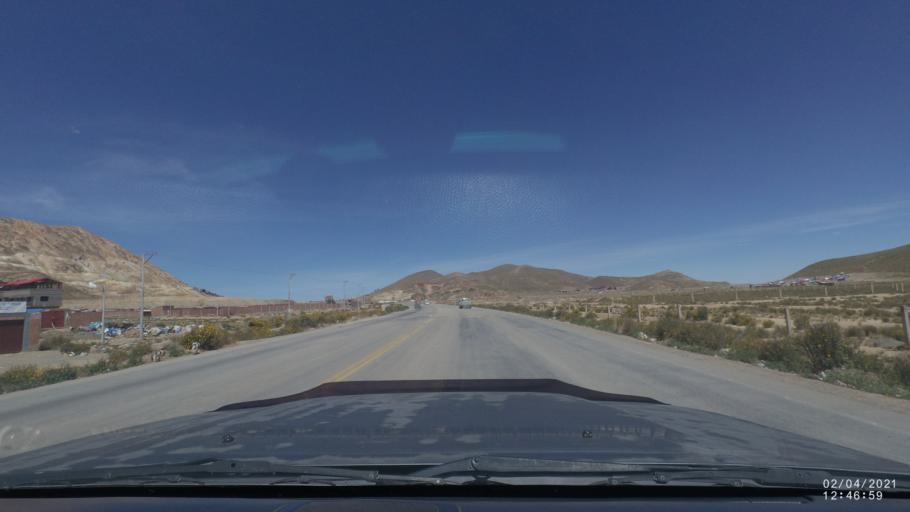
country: BO
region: Oruro
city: Oruro
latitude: -17.9493
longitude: -67.1446
